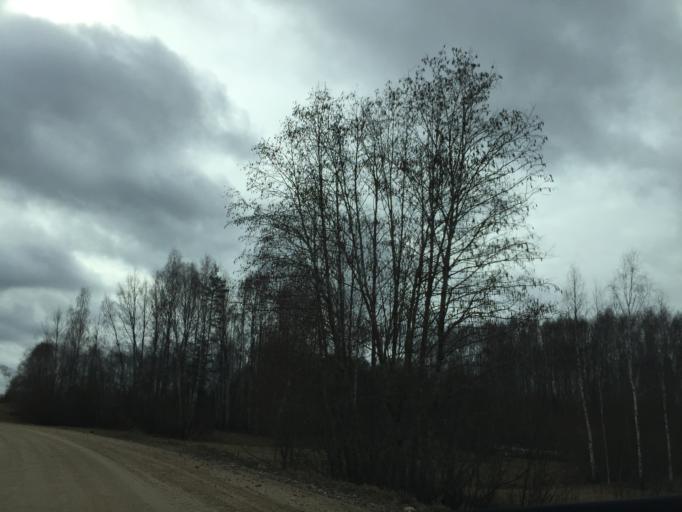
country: LV
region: Kraslavas Rajons
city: Kraslava
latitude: 55.9730
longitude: 27.0784
